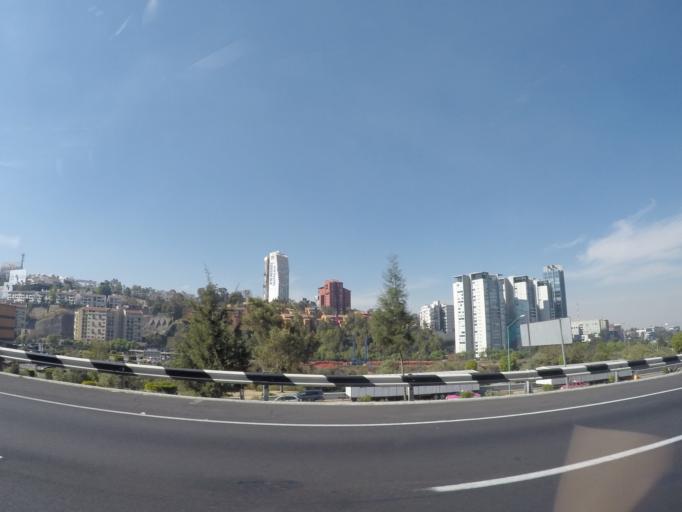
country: MX
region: Mexico City
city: Col. Bosques de las Lomas
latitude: 19.3626
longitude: -99.2681
